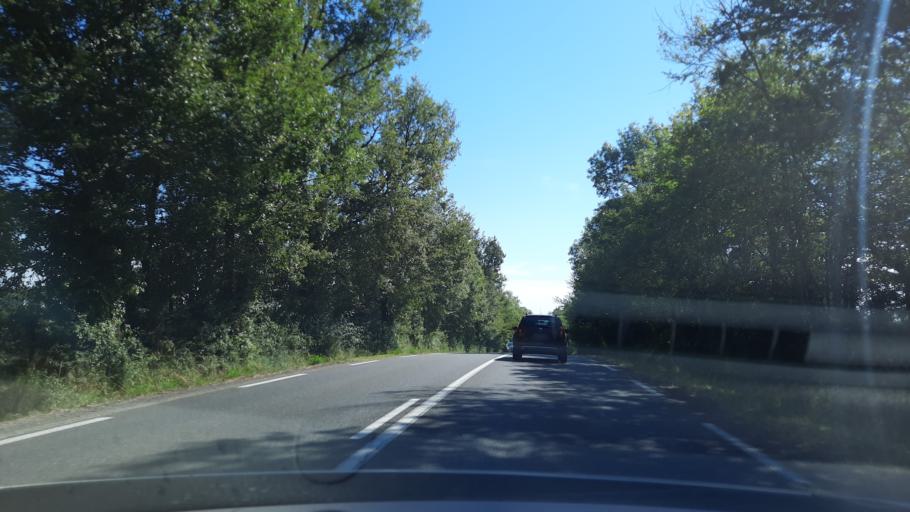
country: FR
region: Midi-Pyrenees
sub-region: Departement de l'Aveyron
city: Villefranche-de-Rouergue
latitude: 44.3269
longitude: 1.9105
